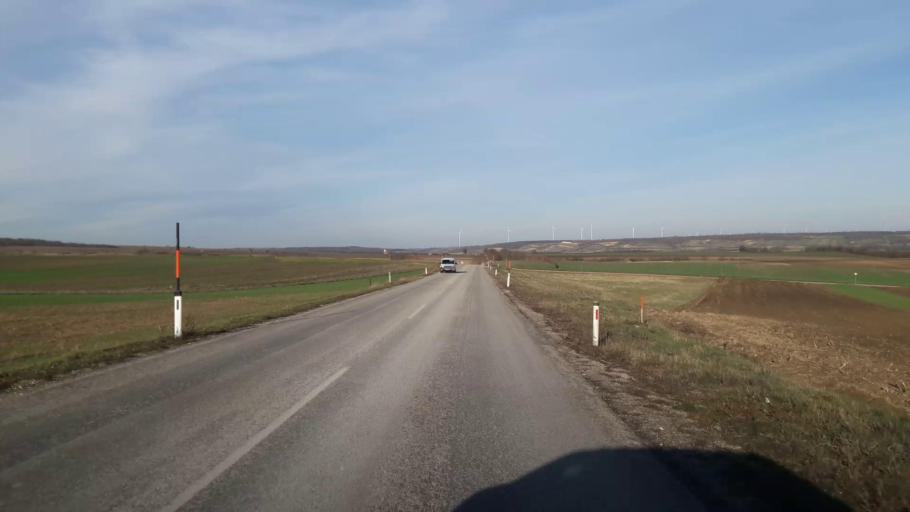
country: AT
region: Lower Austria
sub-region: Politischer Bezirk Ganserndorf
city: Auersthal
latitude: 48.3828
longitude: 16.6301
